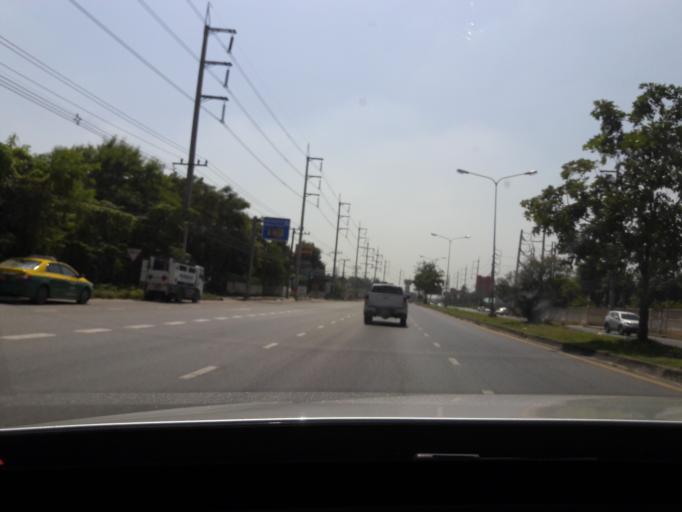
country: TH
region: Samut Sakhon
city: Krathum Baen
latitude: 13.6425
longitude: 100.2993
